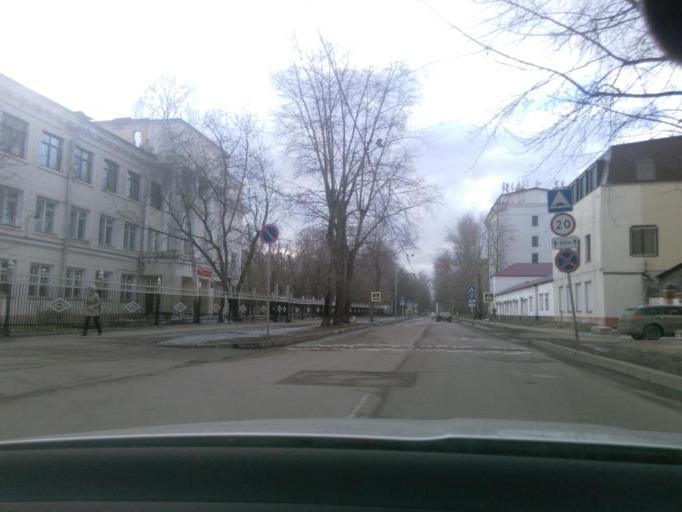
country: RU
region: Moscow
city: Zamoskvorech'ye
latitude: 55.7181
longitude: 37.6136
